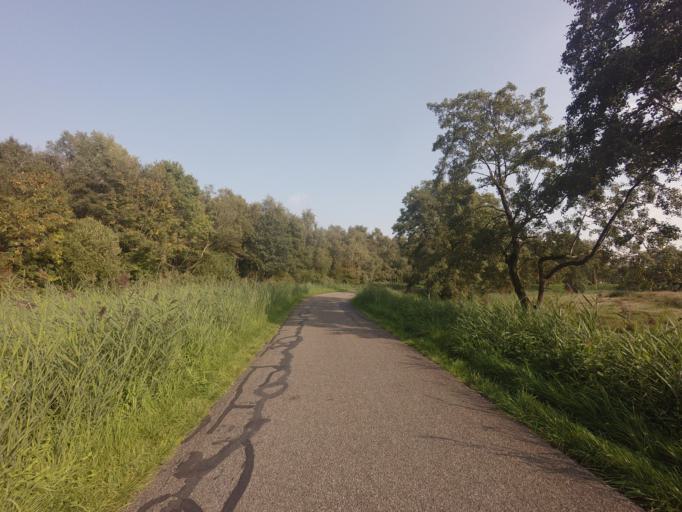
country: NL
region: Groningen
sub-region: Gemeente Haren
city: Haren
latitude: 53.1789
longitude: 6.5759
